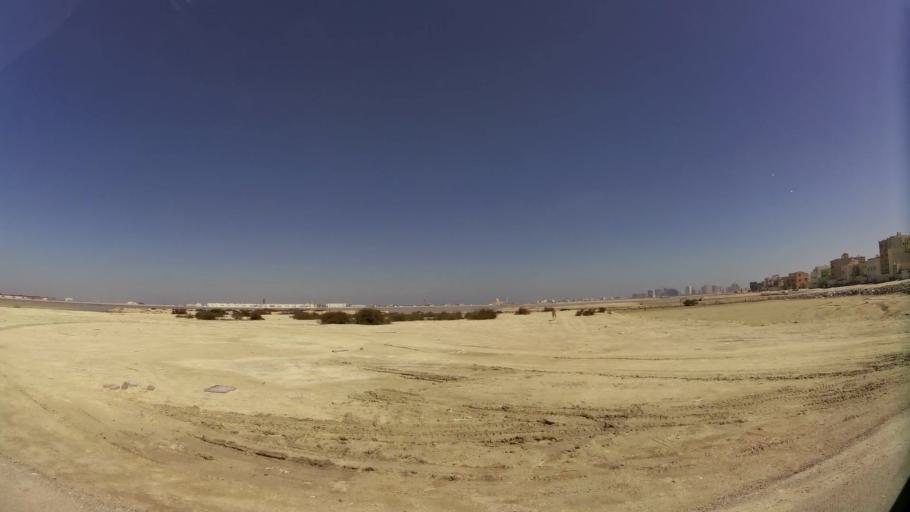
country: BH
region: Muharraq
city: Al Muharraq
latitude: 26.2890
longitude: 50.6250
